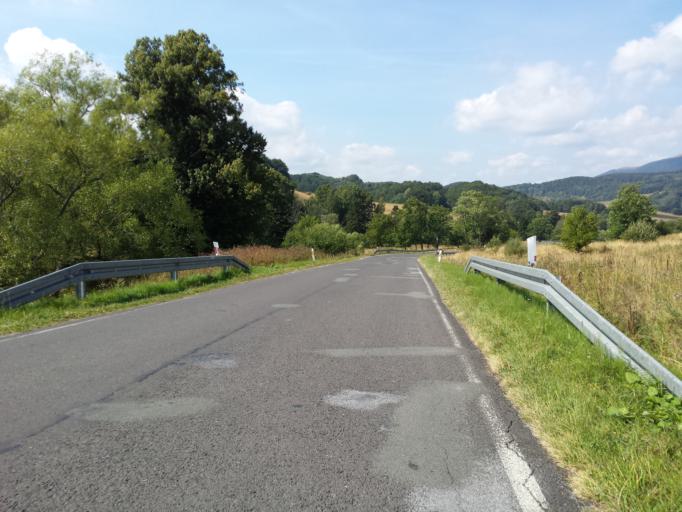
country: PL
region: Subcarpathian Voivodeship
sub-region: Powiat bieszczadzki
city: Lutowiska
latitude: 49.1297
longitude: 22.5818
